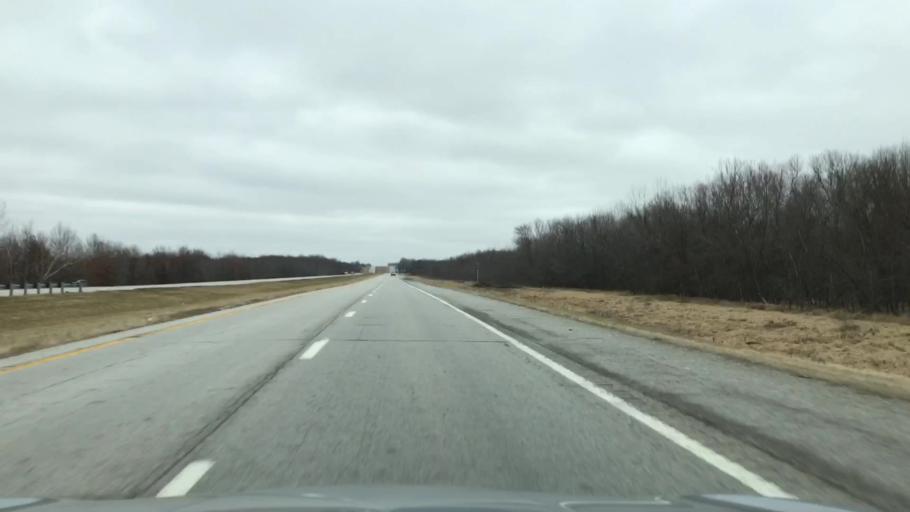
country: US
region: Missouri
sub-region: Linn County
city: Linneus
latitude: 39.7779
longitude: -93.2231
